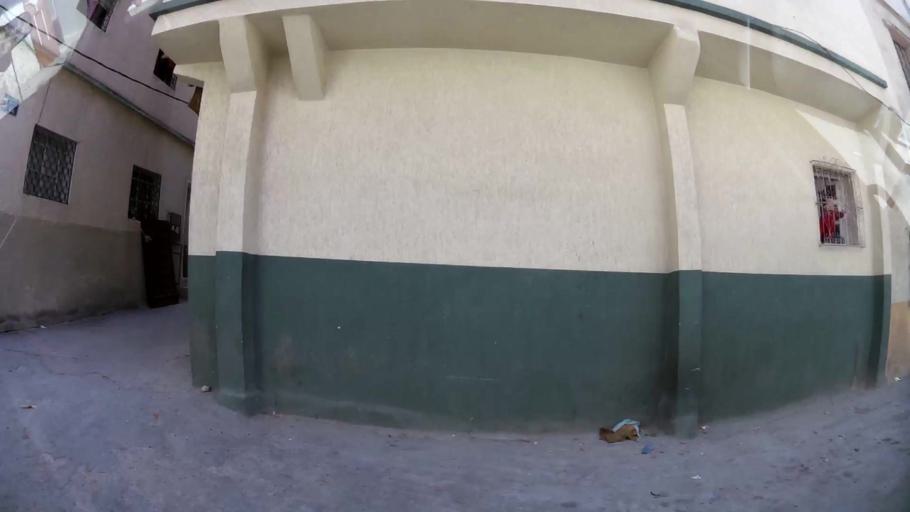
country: MA
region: Tanger-Tetouan
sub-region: Tanger-Assilah
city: Tangier
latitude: 35.7491
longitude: -5.8023
